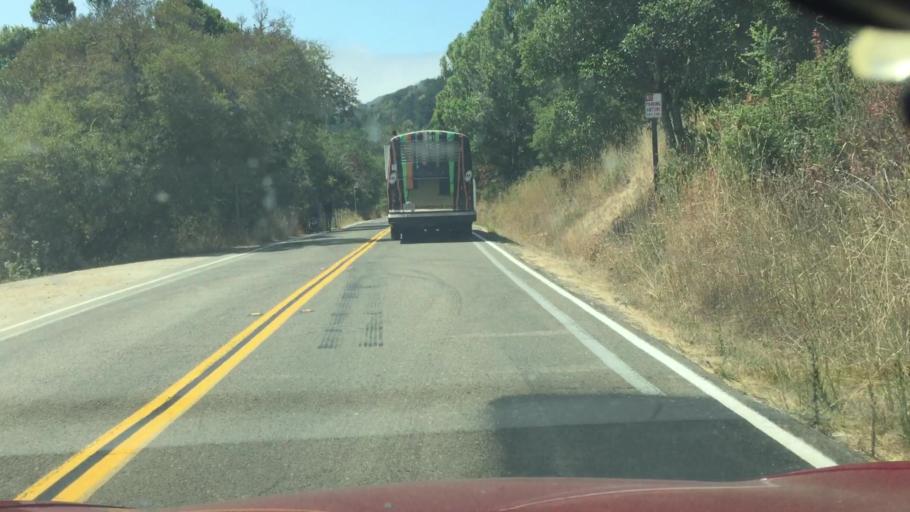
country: US
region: California
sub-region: Marin County
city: Tamalpais Valley
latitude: 37.8836
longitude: -122.5729
